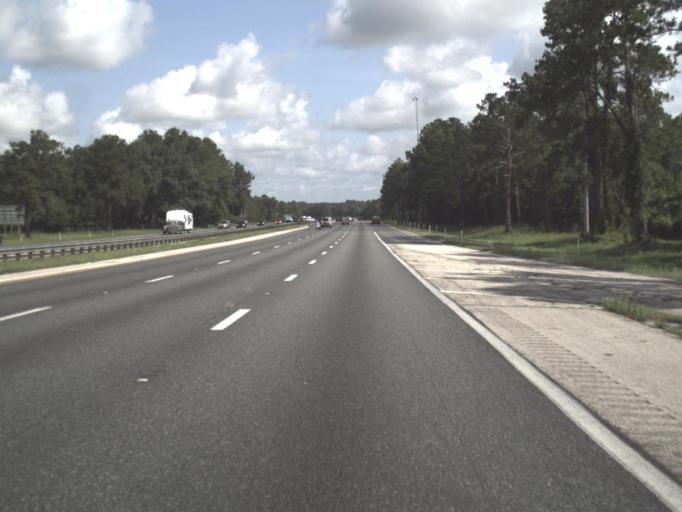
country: US
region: Florida
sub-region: Alachua County
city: Gainesville
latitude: 29.5002
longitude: -82.2961
